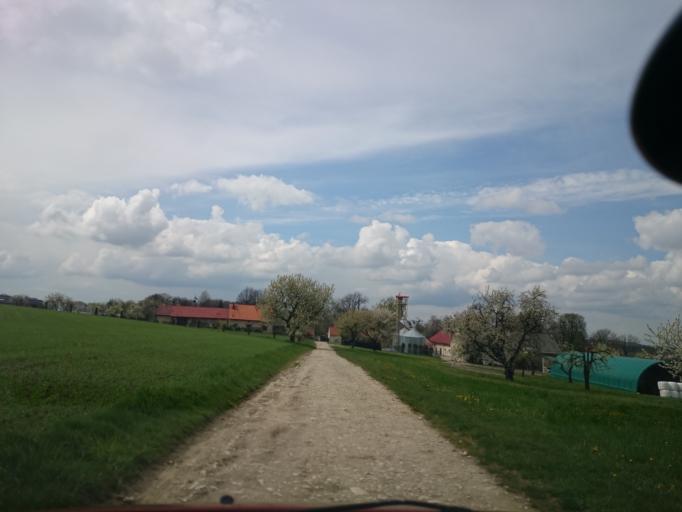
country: PL
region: Opole Voivodeship
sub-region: Powiat krapkowicki
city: Rozwadza
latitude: 50.4895
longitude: 18.1237
